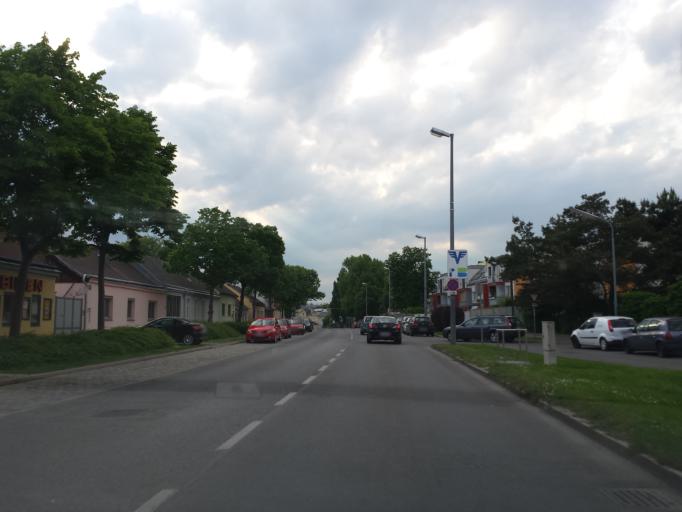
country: AT
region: Lower Austria
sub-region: Politischer Bezirk Ganserndorf
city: Gross-Enzersdorf
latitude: 48.2133
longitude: 16.5285
